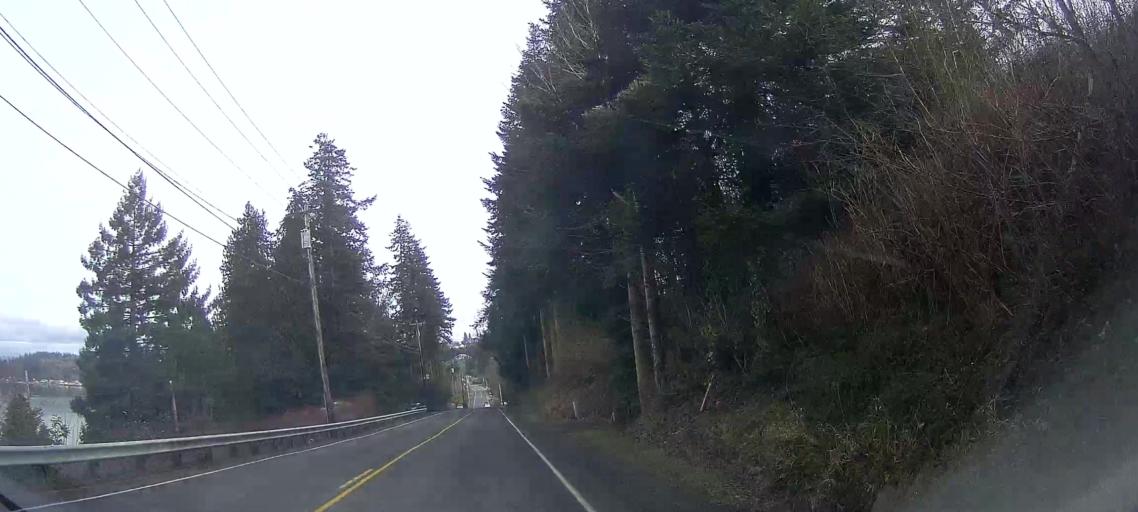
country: US
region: Washington
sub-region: Island County
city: Camano
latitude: 48.2504
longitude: -122.4895
